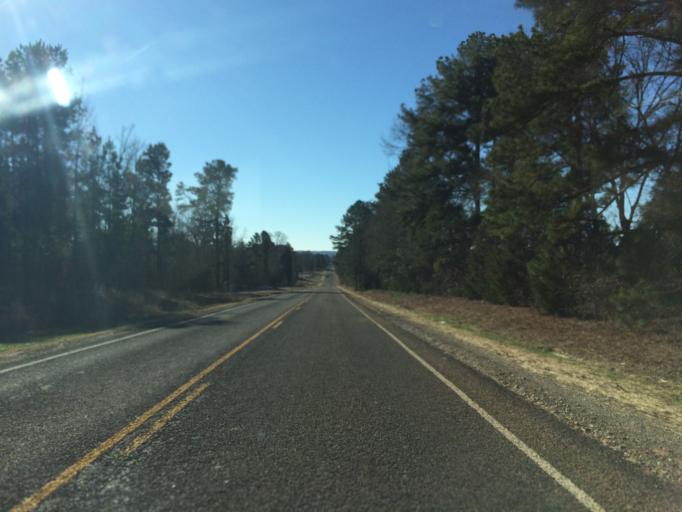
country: US
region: Texas
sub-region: Wood County
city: Hawkins
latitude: 32.6256
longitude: -95.2743
